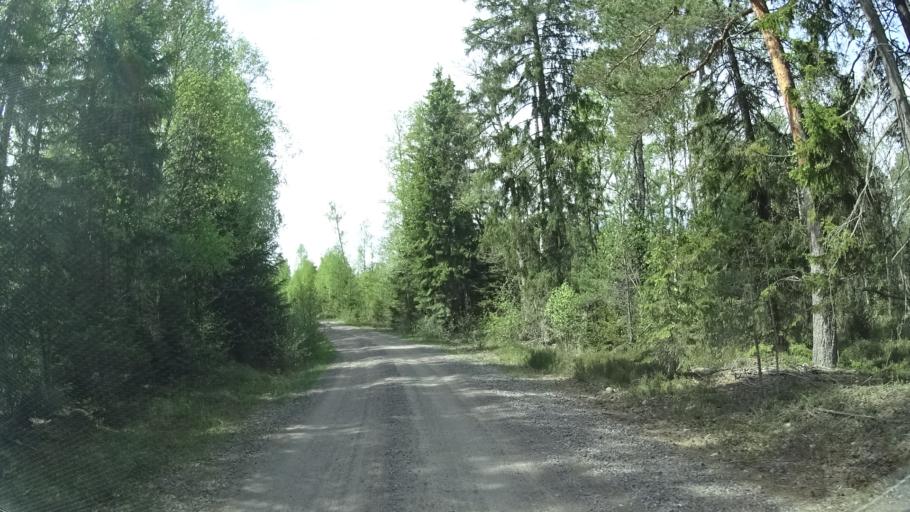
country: SE
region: OEstergoetland
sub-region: Finspangs Kommun
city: Finspang
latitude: 58.7791
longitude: 15.8458
